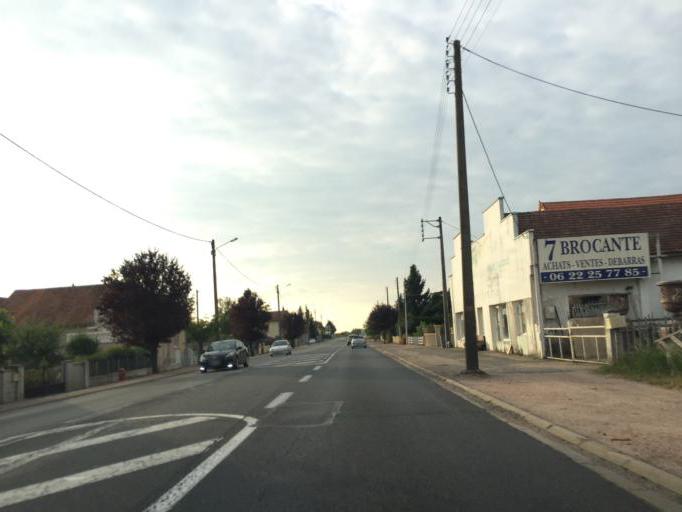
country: FR
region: Auvergne
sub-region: Departement de l'Allier
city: Varennes-sur-Allier
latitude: 46.3520
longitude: 3.3781
